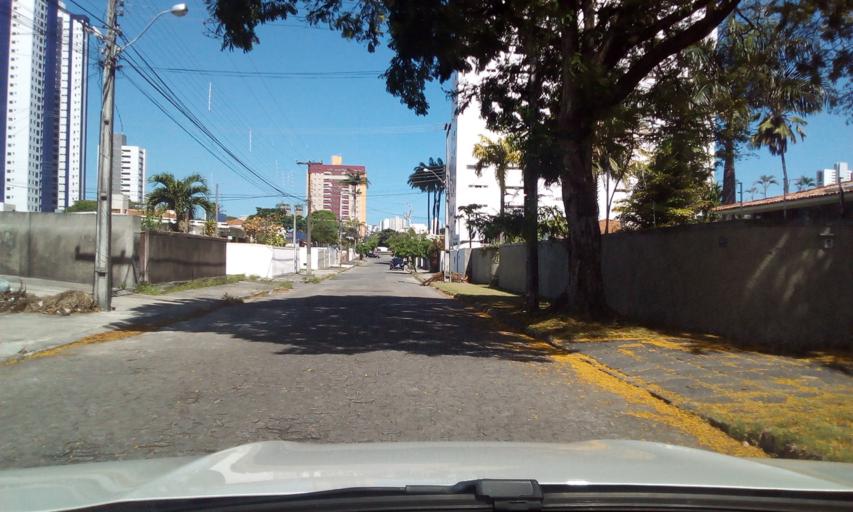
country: BR
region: Paraiba
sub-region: Joao Pessoa
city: Joao Pessoa
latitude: -7.1166
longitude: -34.8569
